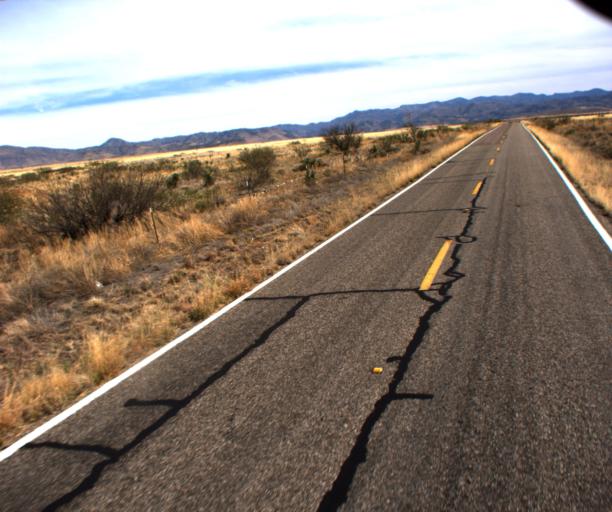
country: US
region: Arizona
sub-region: Cochise County
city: Willcox
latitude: 32.0469
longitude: -109.4879
